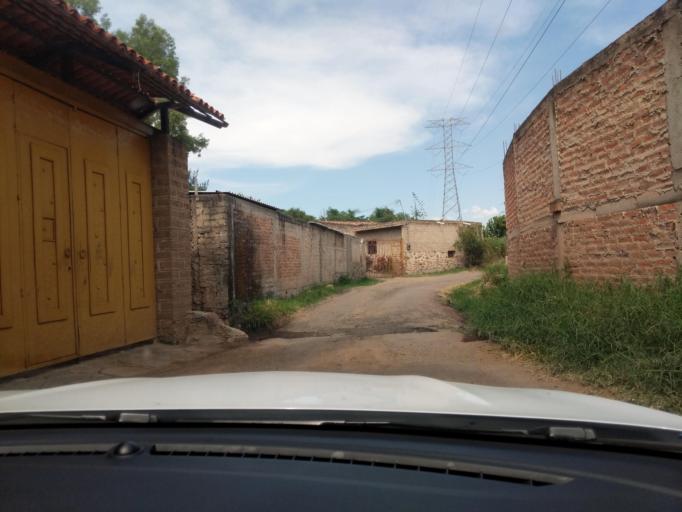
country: MX
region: Jalisco
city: Coyula
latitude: 20.6281
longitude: -103.2147
